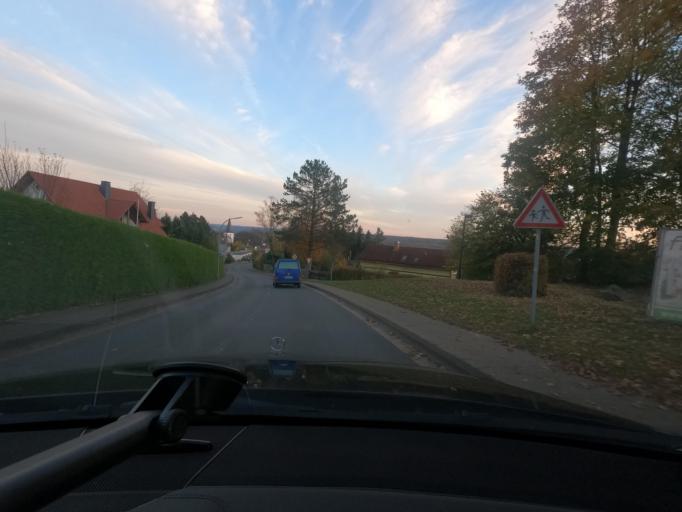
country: DE
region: North Rhine-Westphalia
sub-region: Regierungsbezirk Arnsberg
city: Mohnesee
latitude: 51.4994
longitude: 8.1248
